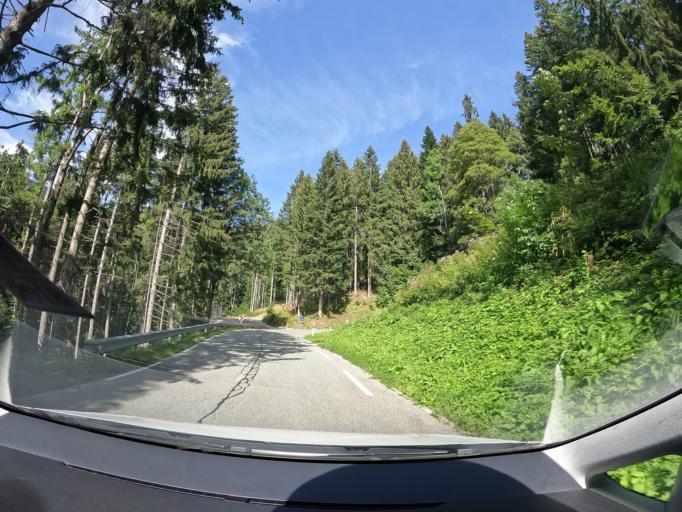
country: AT
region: Carinthia
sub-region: Politischer Bezirk Feldkirchen
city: Glanegg
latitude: 46.7476
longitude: 14.2162
